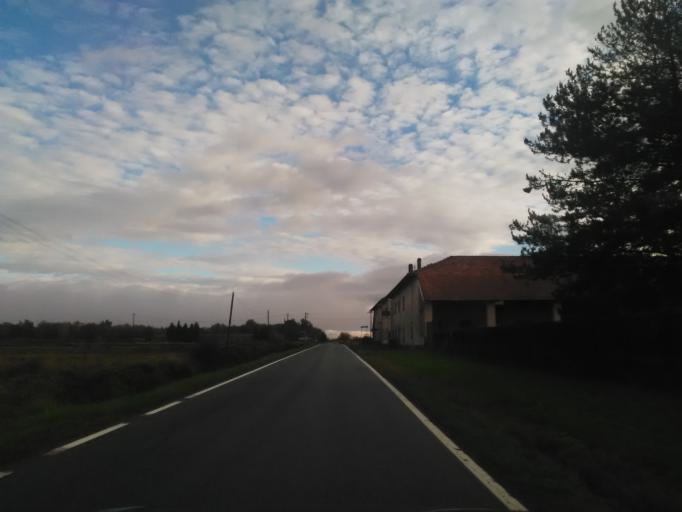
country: IT
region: Piedmont
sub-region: Provincia di Vercelli
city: Rovasenda
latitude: 45.5468
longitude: 8.3452
